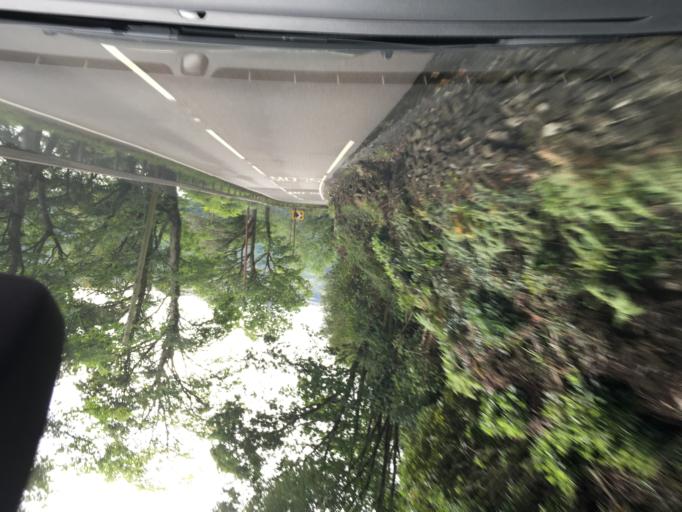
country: GB
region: Scotland
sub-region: Argyll and Bute
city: Garelochhead
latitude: 56.2131
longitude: -4.6969
